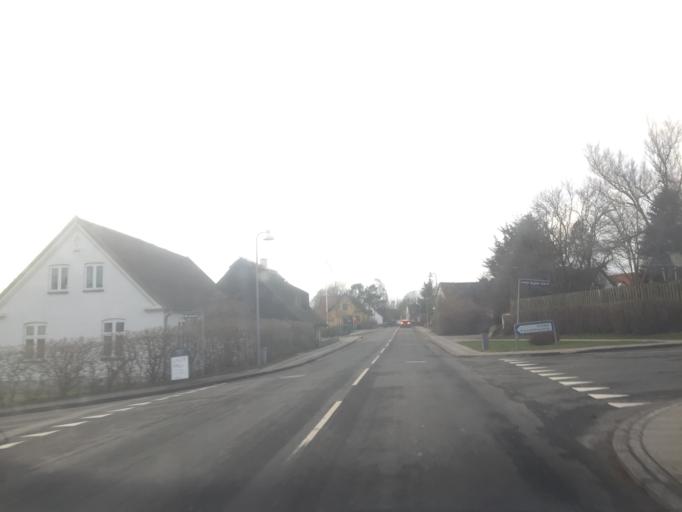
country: DK
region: Capital Region
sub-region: Egedal Kommune
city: Smorumnedre
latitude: 55.7102
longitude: 12.3011
